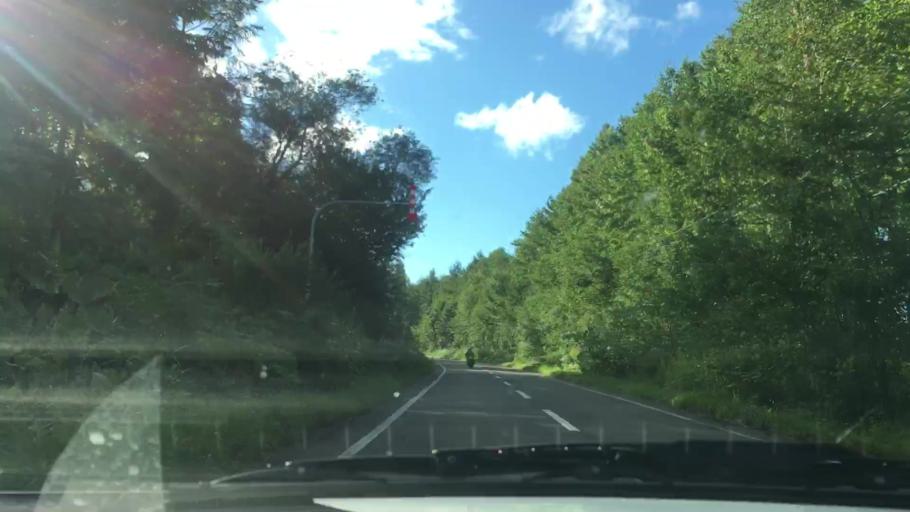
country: JP
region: Hokkaido
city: Otofuke
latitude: 43.1721
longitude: 142.9740
